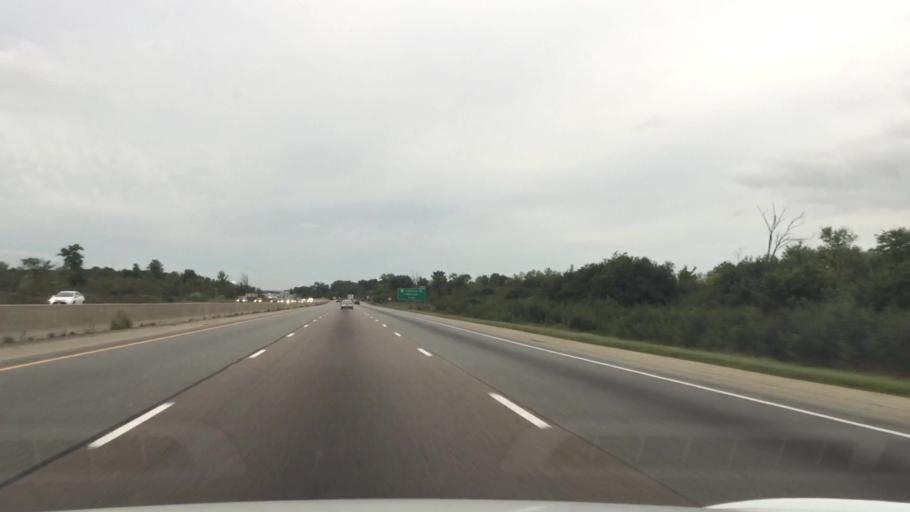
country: CA
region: Ontario
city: Cambridge
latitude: 43.4304
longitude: -80.2632
